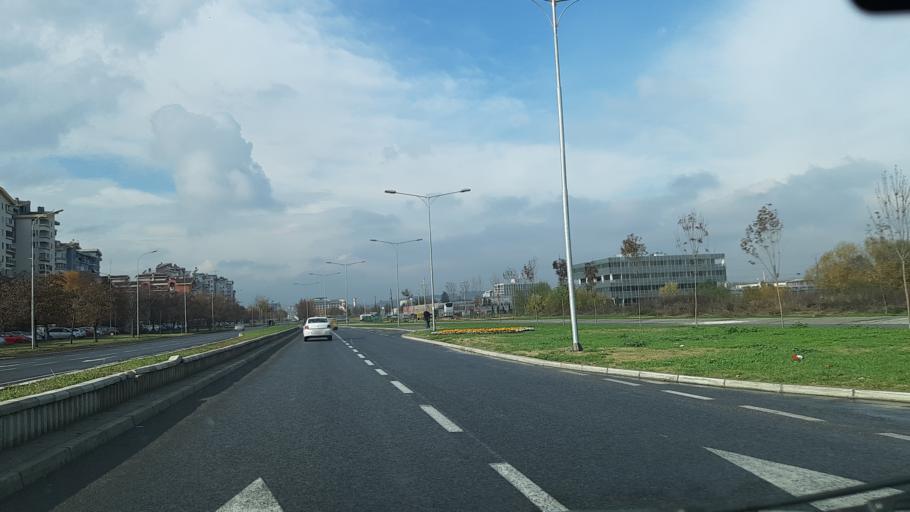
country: MK
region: Kisela Voda
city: Usje
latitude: 41.9855
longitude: 21.4836
